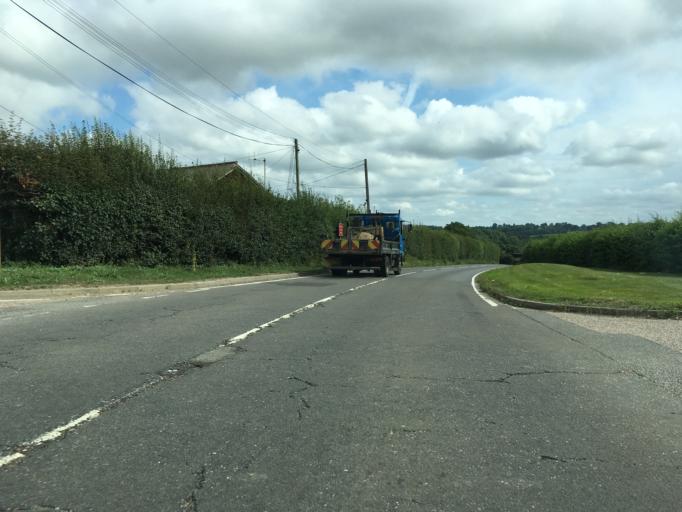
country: GB
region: England
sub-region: Kent
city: Marden
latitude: 51.1113
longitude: 0.4315
